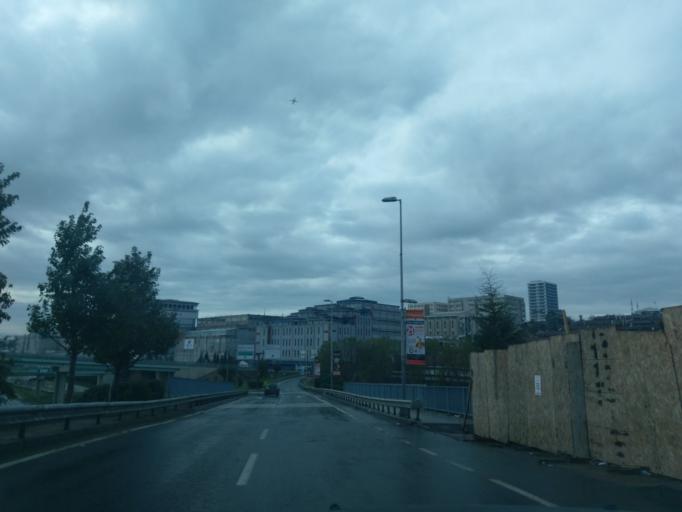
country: TR
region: Istanbul
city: Basaksehir
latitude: 41.0838
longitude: 28.8108
